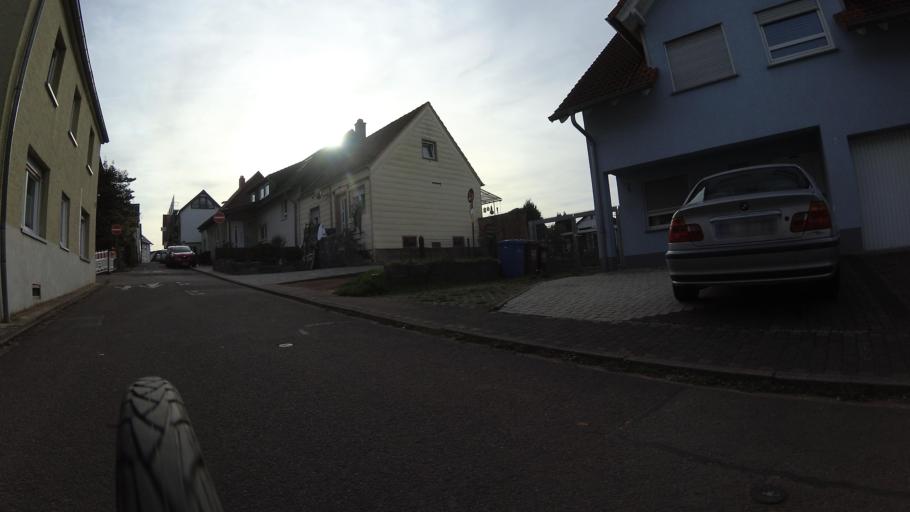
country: DE
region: Rheinland-Pfalz
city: Ramstein-Miesenbach
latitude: 49.4453
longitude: 7.5598
